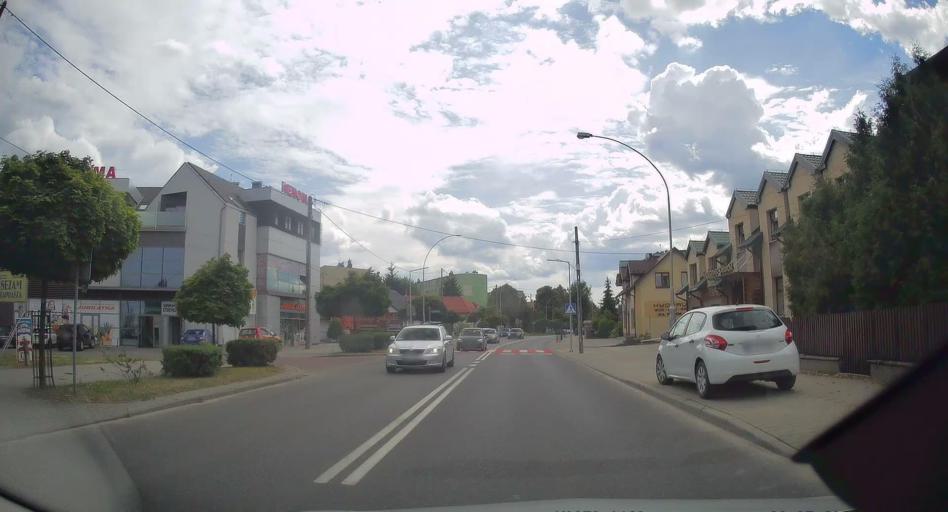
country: PL
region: Subcarpathian Voivodeship
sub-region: Powiat debicki
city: Debica
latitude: 50.0459
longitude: 21.4037
